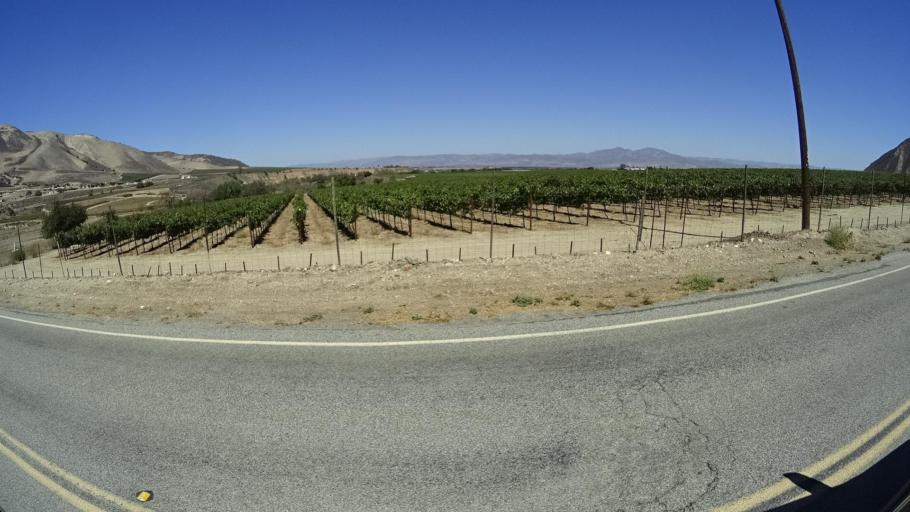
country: US
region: California
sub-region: Monterey County
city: Greenfield
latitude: 36.2786
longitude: -121.3130
